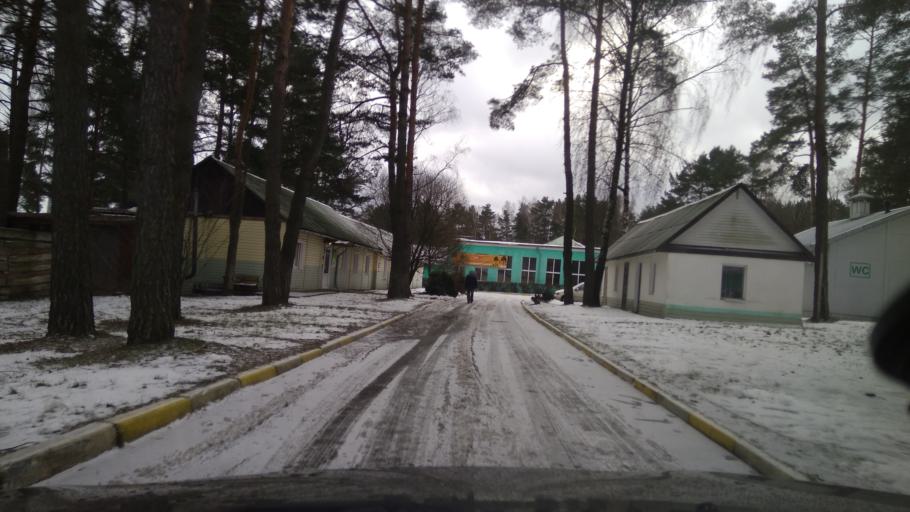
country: BY
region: Minsk
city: Borovlyany
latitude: 53.9613
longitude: 27.6501
